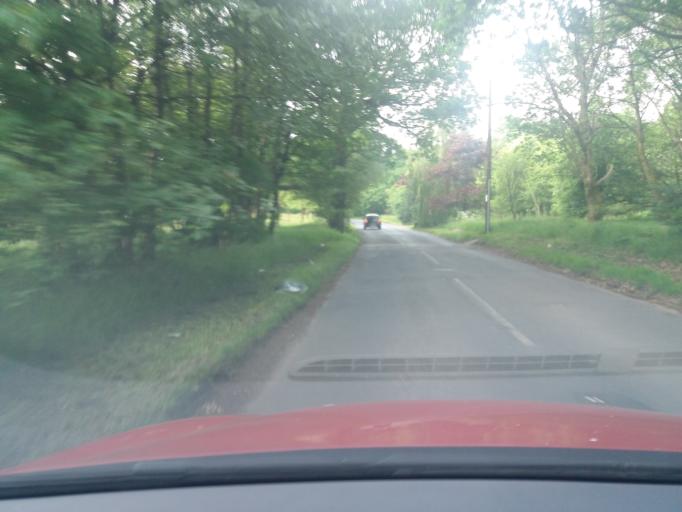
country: GB
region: England
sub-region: Borough of Bolton
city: Horwich
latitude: 53.6213
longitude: -2.5628
